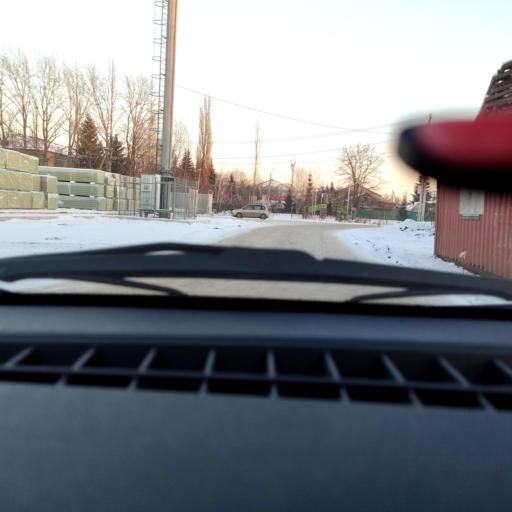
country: RU
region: Bashkortostan
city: Ufa
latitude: 54.6160
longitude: 55.8986
